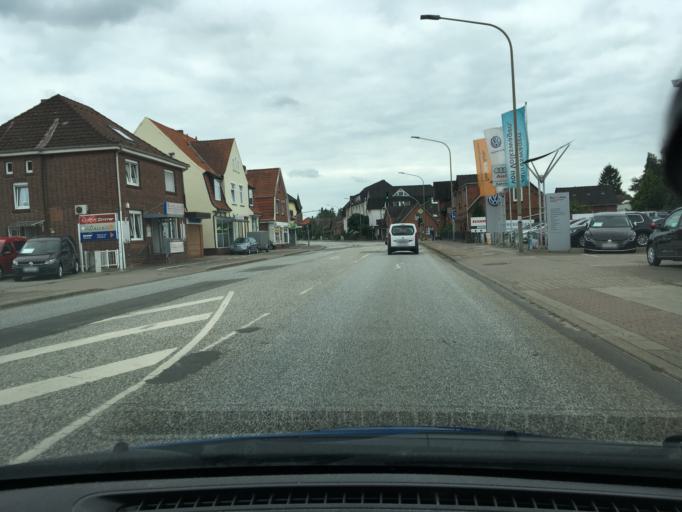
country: DE
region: Schleswig-Holstein
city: Geesthacht
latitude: 53.4438
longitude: 10.3630
